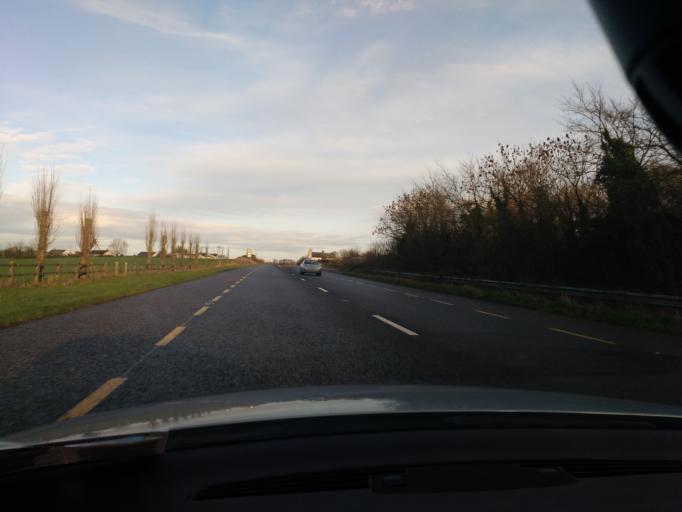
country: IE
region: Munster
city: Thurles
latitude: 52.6465
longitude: -7.7252
